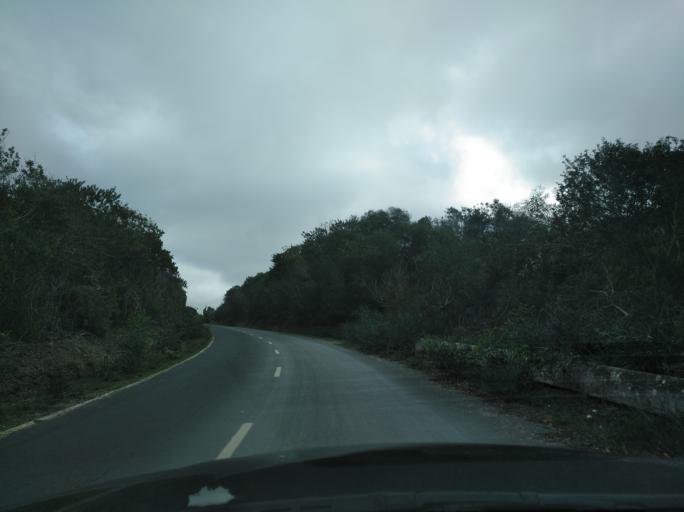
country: PT
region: Beja
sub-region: Odemira
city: Vila Nova de Milfontes
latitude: 37.7176
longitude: -8.7820
